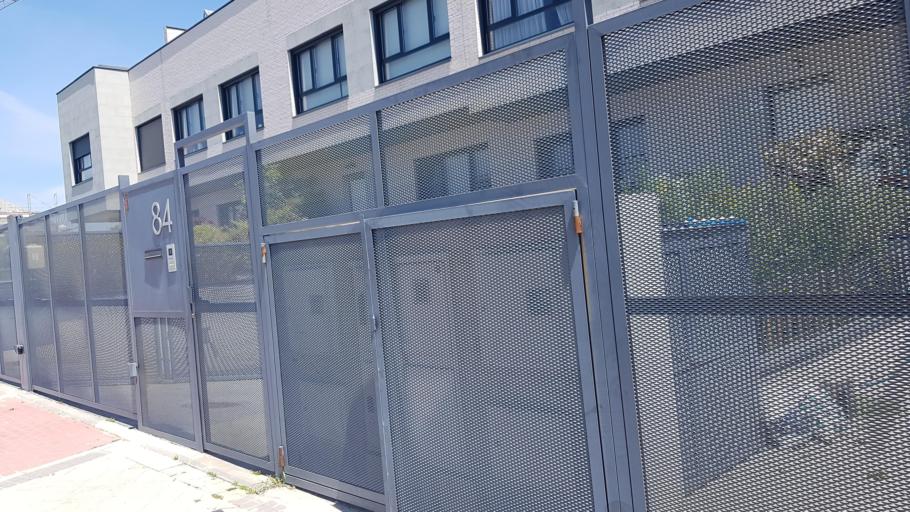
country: ES
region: Madrid
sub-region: Provincia de Madrid
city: Hortaleza
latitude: 40.4815
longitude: -3.6365
